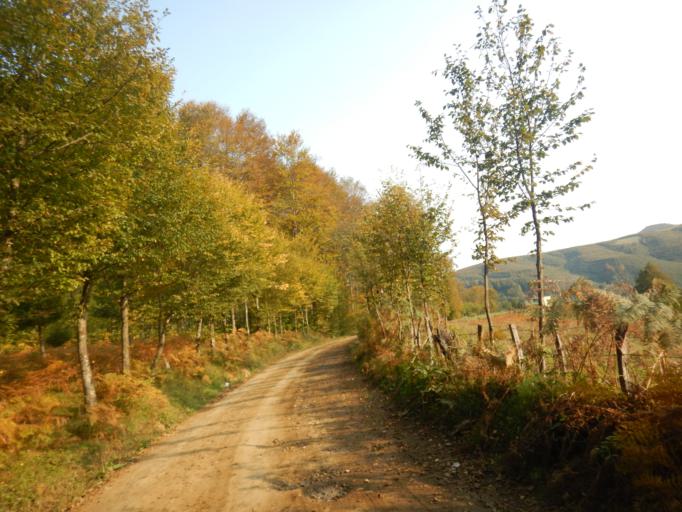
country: TR
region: Ordu
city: Golkoy
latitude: 40.6580
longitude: 37.5586
